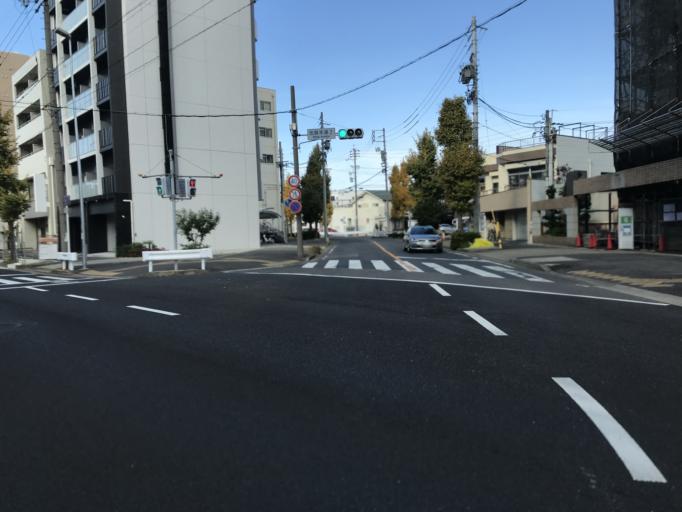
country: JP
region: Aichi
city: Nagoya-shi
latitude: 35.1964
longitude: 136.9212
